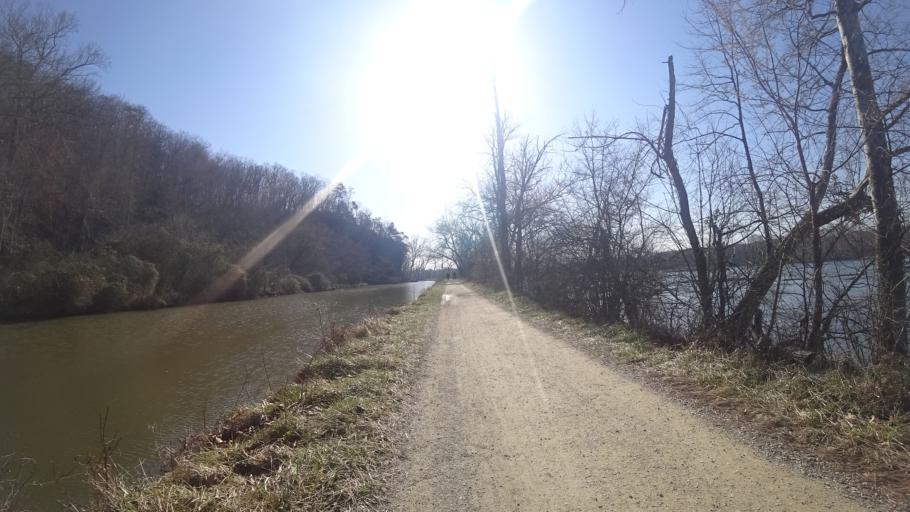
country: US
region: Virginia
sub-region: Loudoun County
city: Lowes Island
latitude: 39.0592
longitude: -77.3159
